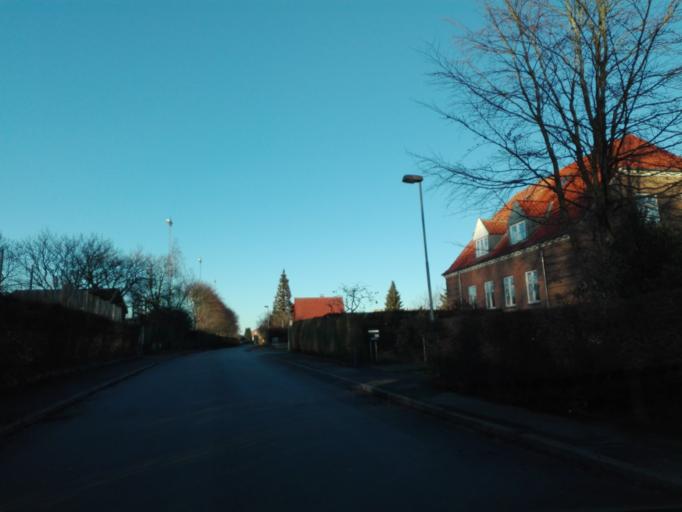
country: DK
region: Central Jutland
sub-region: Arhus Kommune
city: Arhus
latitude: 56.1788
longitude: 10.2126
